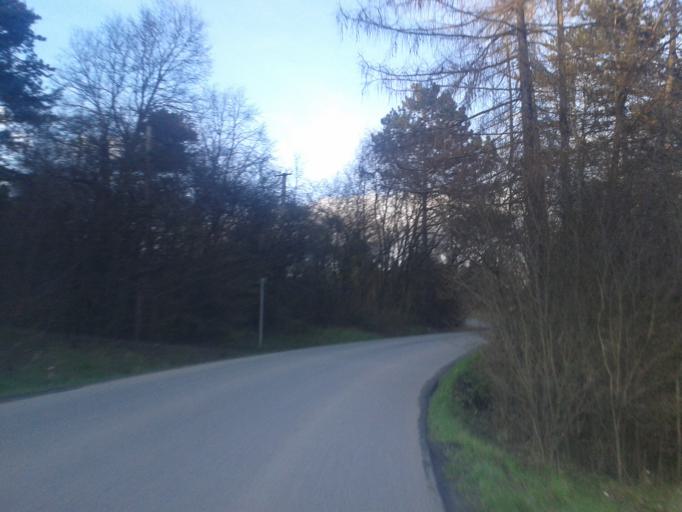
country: CZ
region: Central Bohemia
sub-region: Okres Beroun
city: Kraluv Dvur
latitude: 49.9222
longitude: 14.0382
